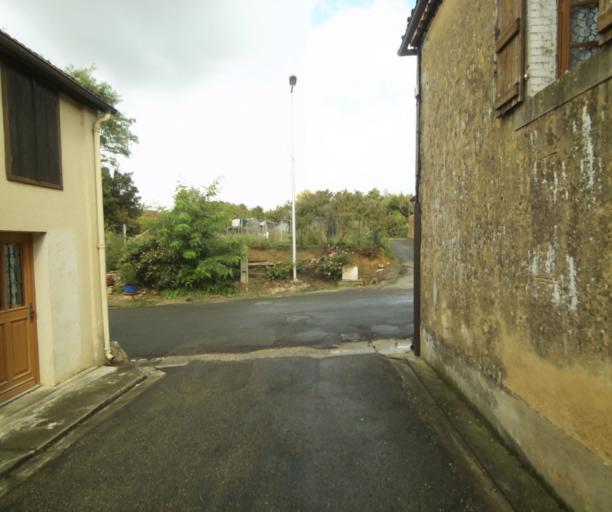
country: FR
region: Midi-Pyrenees
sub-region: Departement du Gers
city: Nogaro
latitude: 43.8211
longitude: -0.0891
